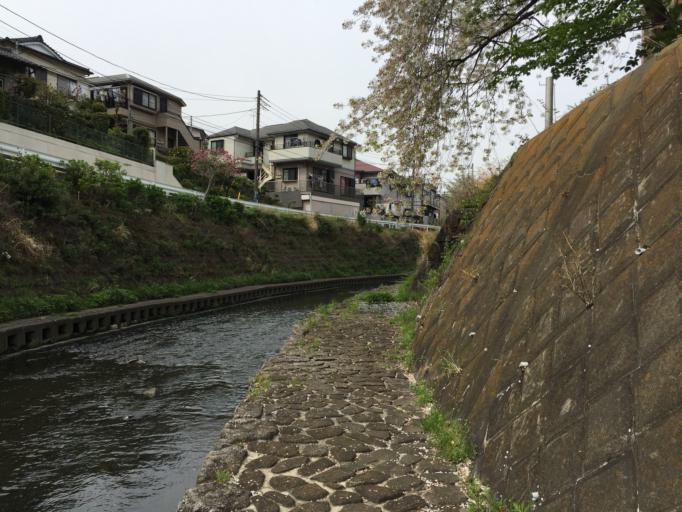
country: JP
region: Kanagawa
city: Yokohama
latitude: 35.4052
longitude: 139.5930
